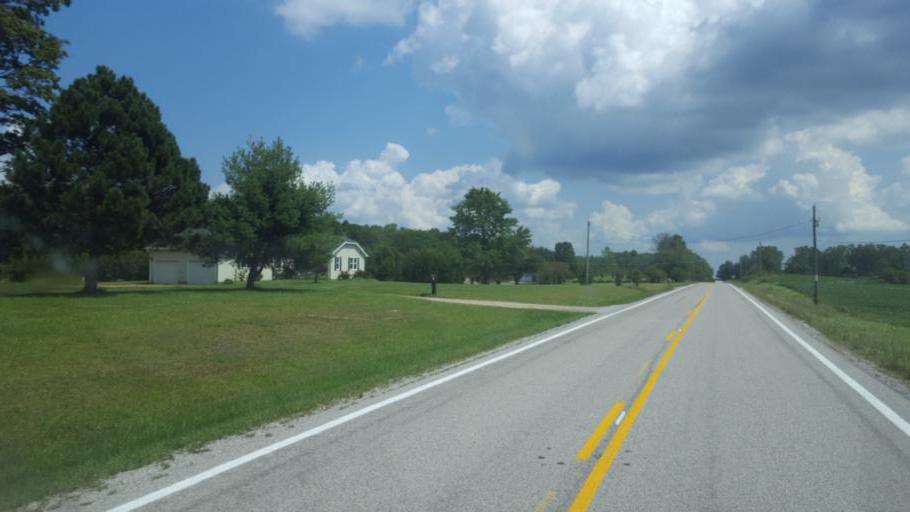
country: US
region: Ohio
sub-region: Knox County
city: Centerburg
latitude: 40.3978
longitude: -82.6725
